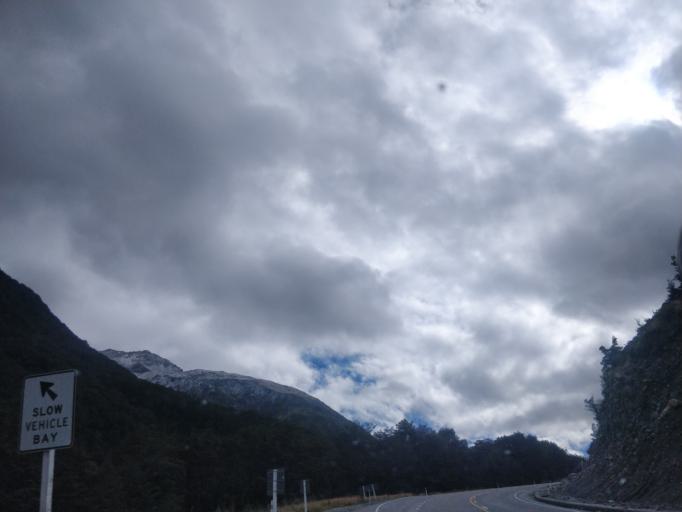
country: NZ
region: West Coast
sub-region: Grey District
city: Greymouth
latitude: -42.9241
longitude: 171.5572
